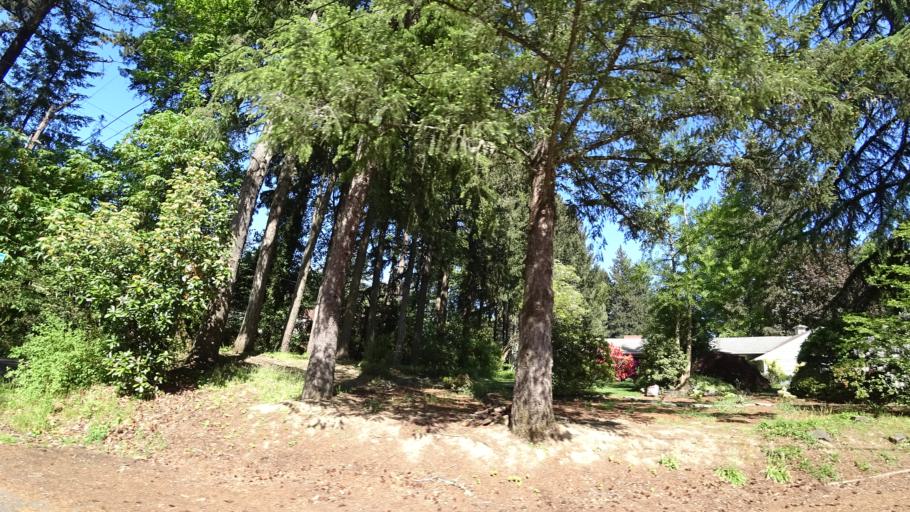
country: US
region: Oregon
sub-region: Washington County
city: Raleigh Hills
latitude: 45.4907
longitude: -122.7396
